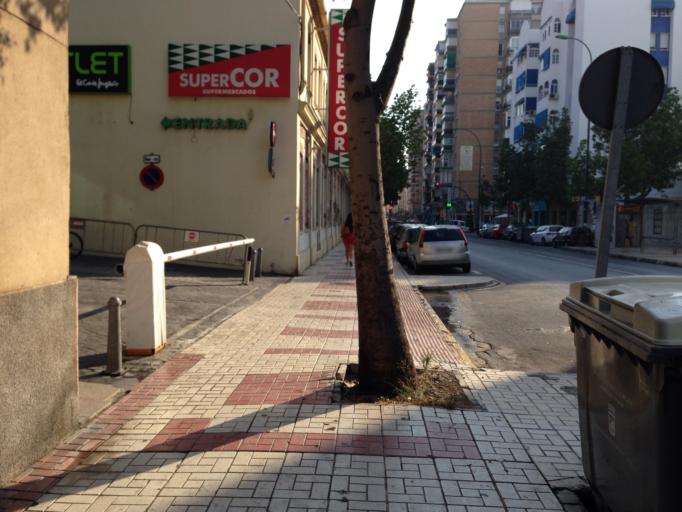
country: ES
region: Andalusia
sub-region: Provincia de Malaga
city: Malaga
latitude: 36.7096
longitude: -4.4318
